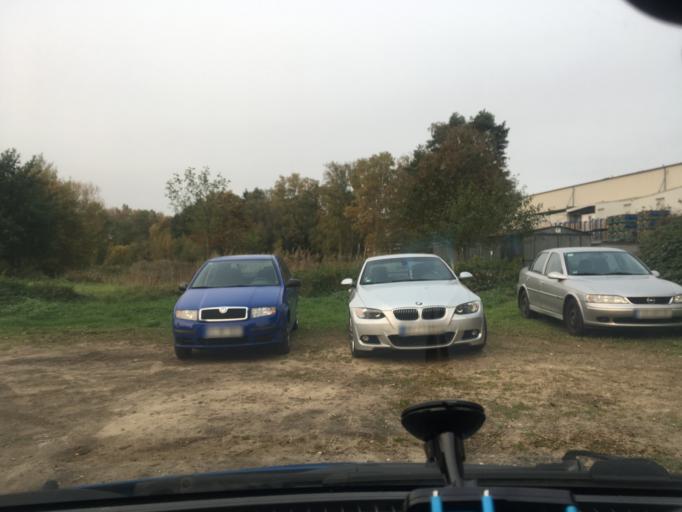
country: DE
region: Lower Saxony
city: Adendorf
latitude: 53.2762
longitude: 10.4189
